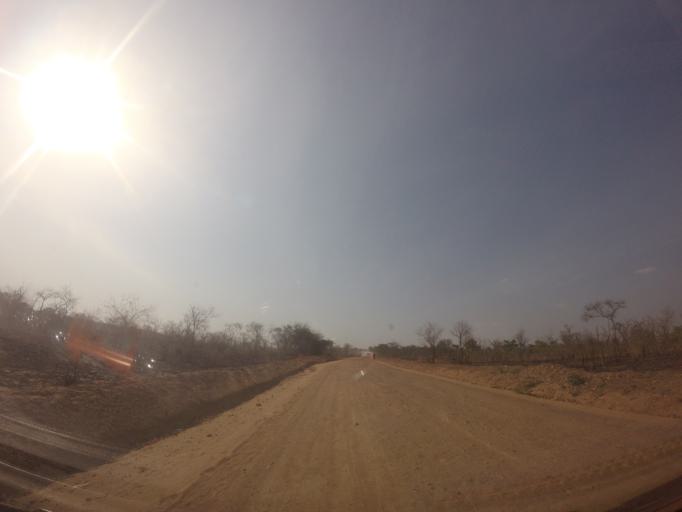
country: UG
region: Northern Region
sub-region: Maracha District
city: Maracha
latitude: 3.1108
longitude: 31.1984
